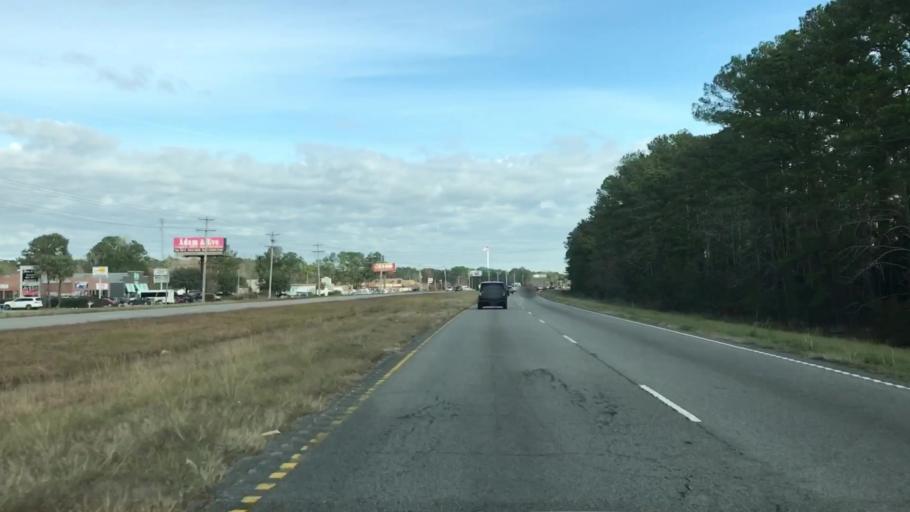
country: US
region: South Carolina
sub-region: Horry County
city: Garden City
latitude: 33.5925
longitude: -79.0251
